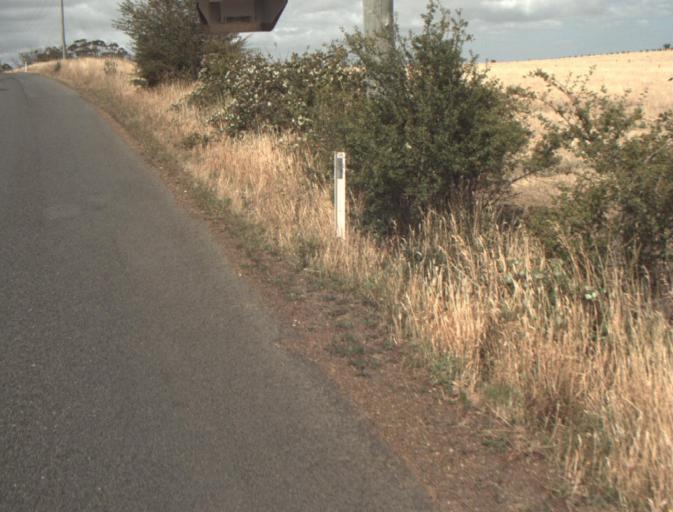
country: AU
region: Tasmania
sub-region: Northern Midlands
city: Evandale
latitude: -41.5112
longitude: 147.2891
